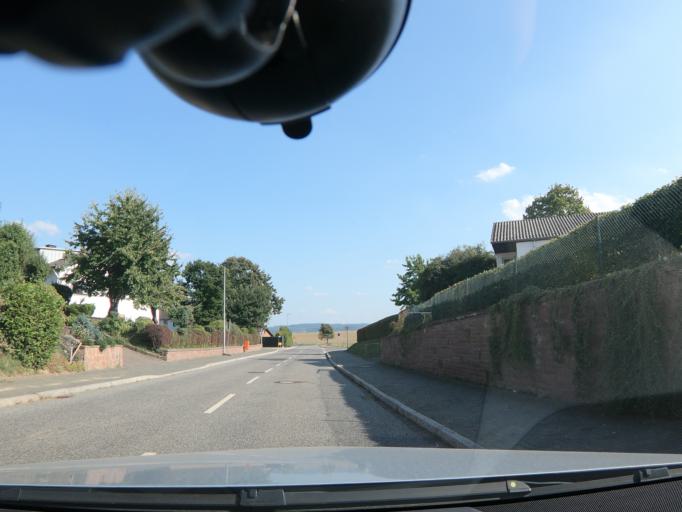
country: DE
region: Hesse
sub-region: Regierungsbezirk Giessen
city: Ebsdorfergrund
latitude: 50.7861
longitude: 8.8348
